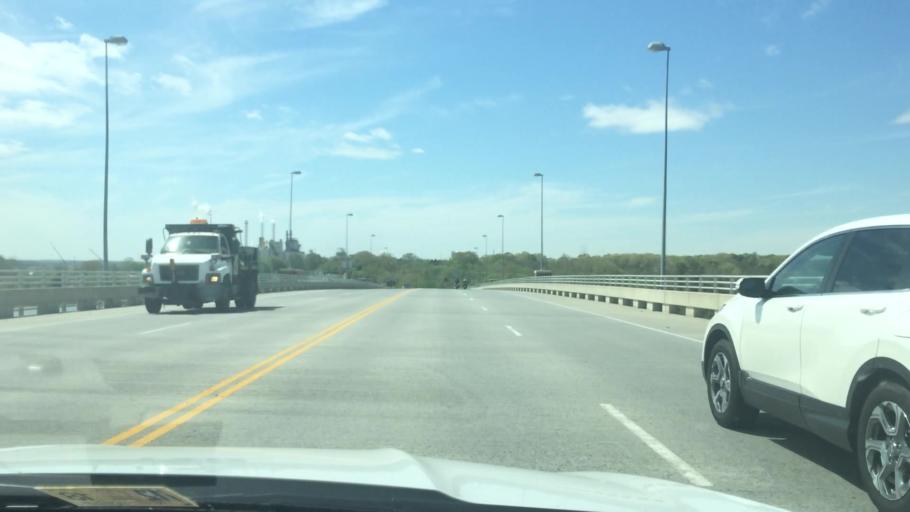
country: US
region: Virginia
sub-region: King William County
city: West Point
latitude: 37.5373
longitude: -76.7888
